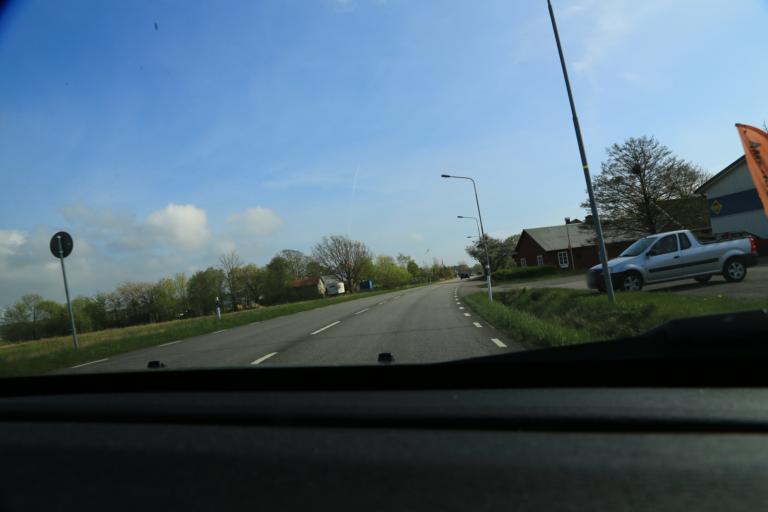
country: SE
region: Halland
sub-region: Varbergs Kommun
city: Veddige
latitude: 57.2221
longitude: 12.2215
